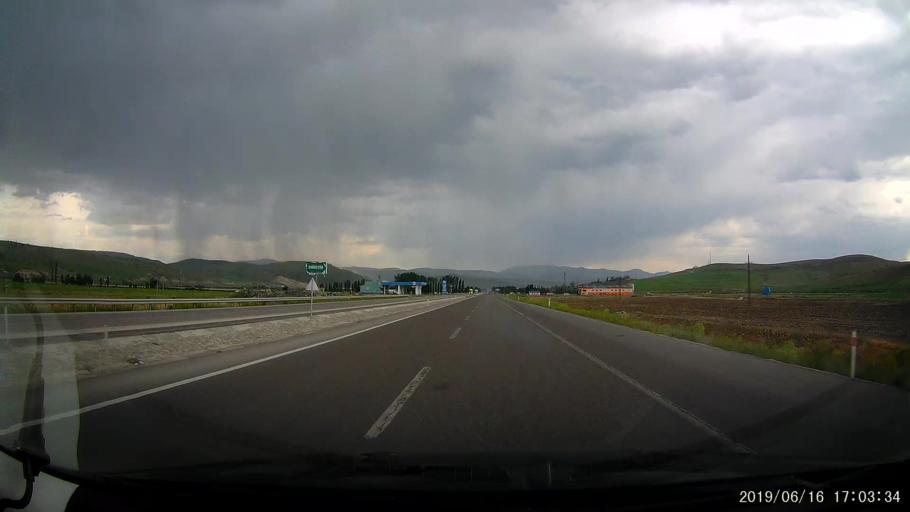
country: TR
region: Erzurum
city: Askale
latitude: 39.9355
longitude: 40.7287
